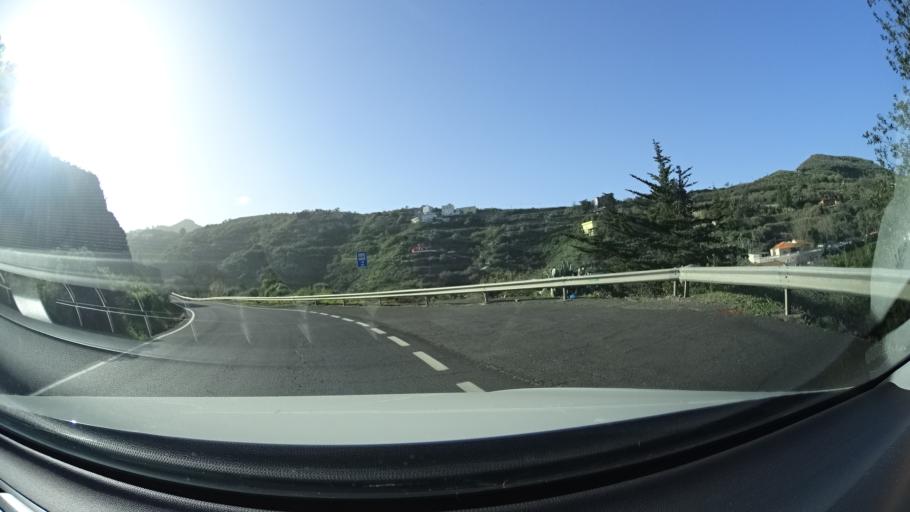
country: ES
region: Canary Islands
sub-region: Provincia de Las Palmas
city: Vega de San Mateo
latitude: 28.0263
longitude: -15.5511
